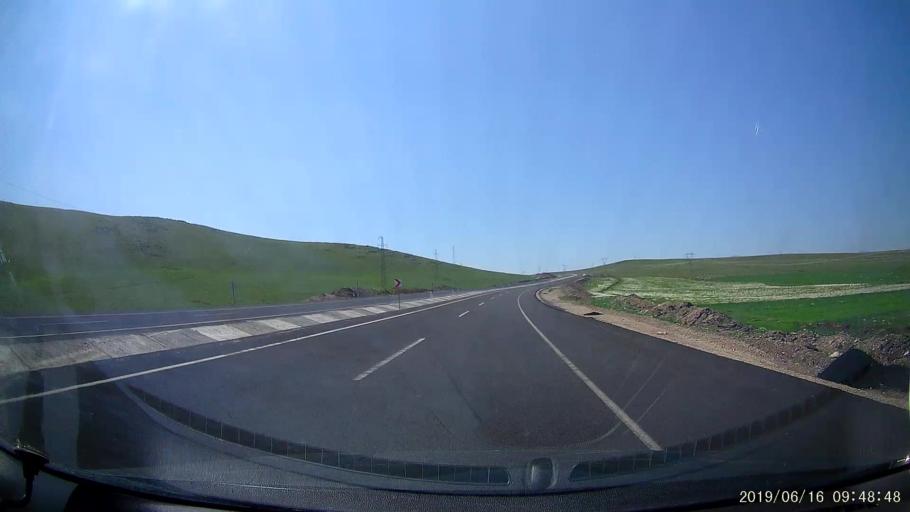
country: TR
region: Kars
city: Digor
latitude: 40.4294
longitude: 43.3558
